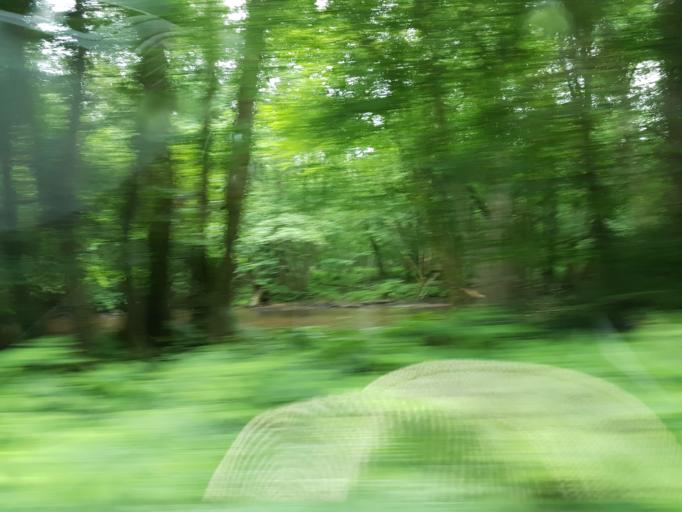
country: FR
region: Bourgogne
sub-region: Departement de la Nievre
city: Corbigny
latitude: 47.1795
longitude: 3.7497
